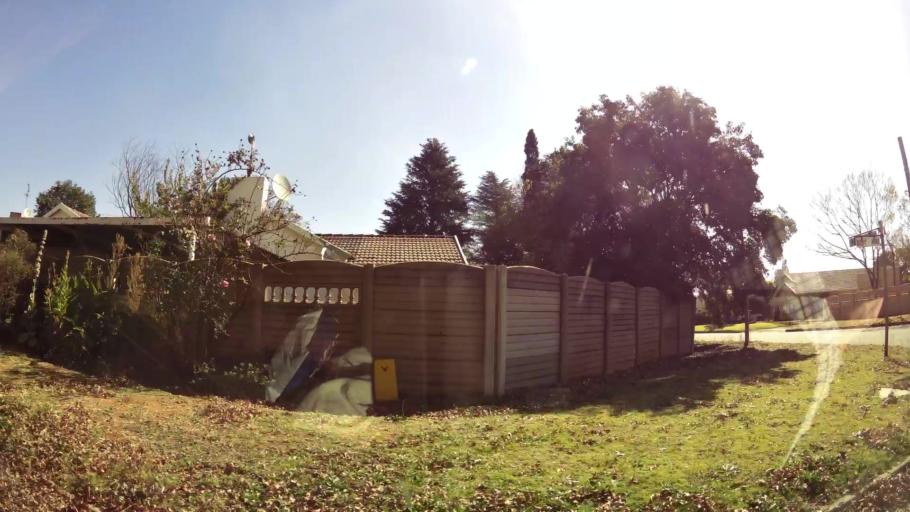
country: ZA
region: Gauteng
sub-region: City of Johannesburg Metropolitan Municipality
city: Modderfontein
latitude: -26.0559
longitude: 28.2050
